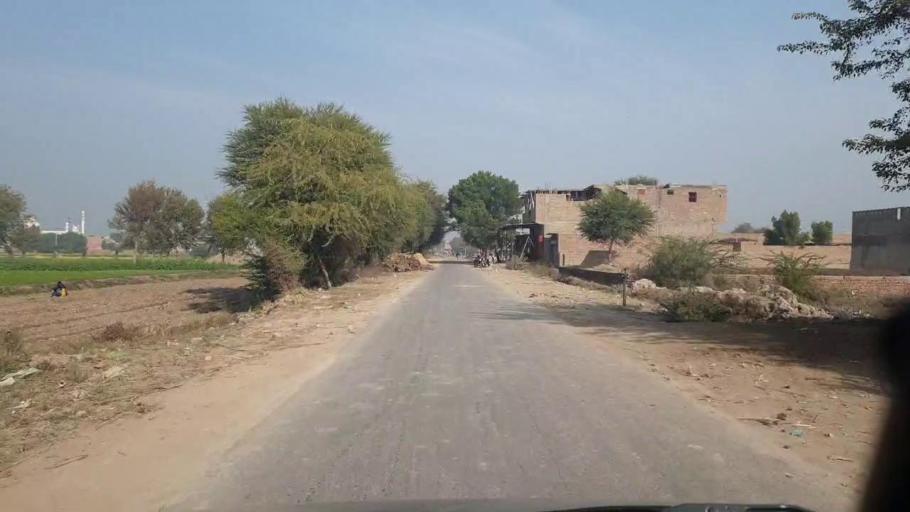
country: PK
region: Sindh
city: Shahdadpur
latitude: 26.0234
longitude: 68.5463
